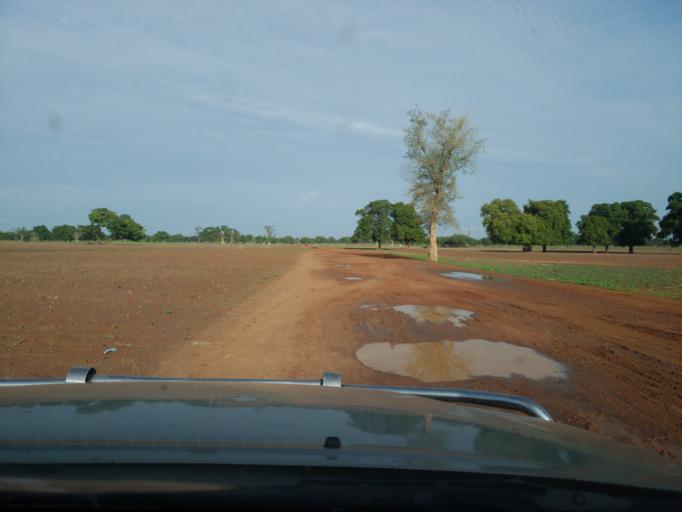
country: ML
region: Sikasso
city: Koutiala
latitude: 12.4214
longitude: -5.6902
